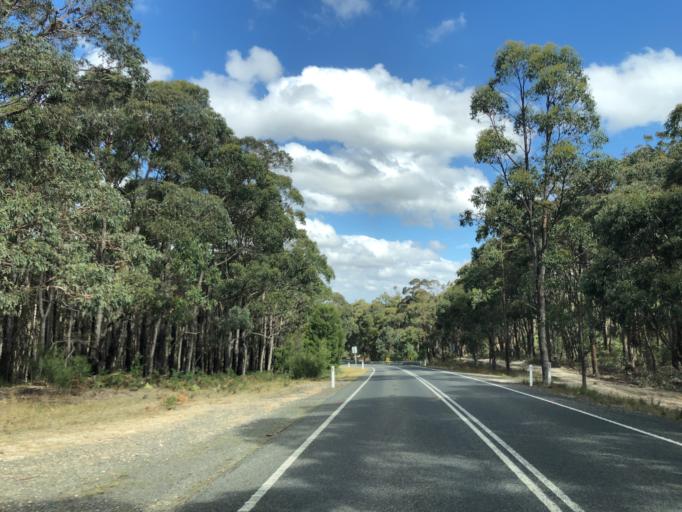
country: AU
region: Victoria
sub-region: Moorabool
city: Bacchus Marsh
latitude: -37.5076
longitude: 144.3110
